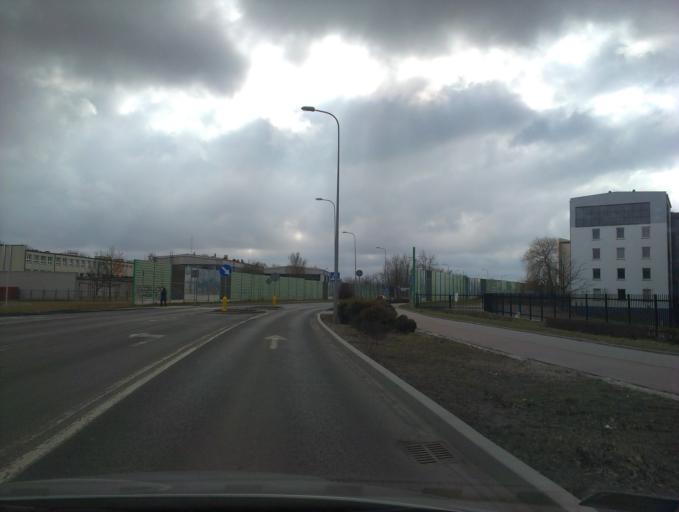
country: PL
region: West Pomeranian Voivodeship
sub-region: Koszalin
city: Koszalin
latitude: 54.1886
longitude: 16.1944
